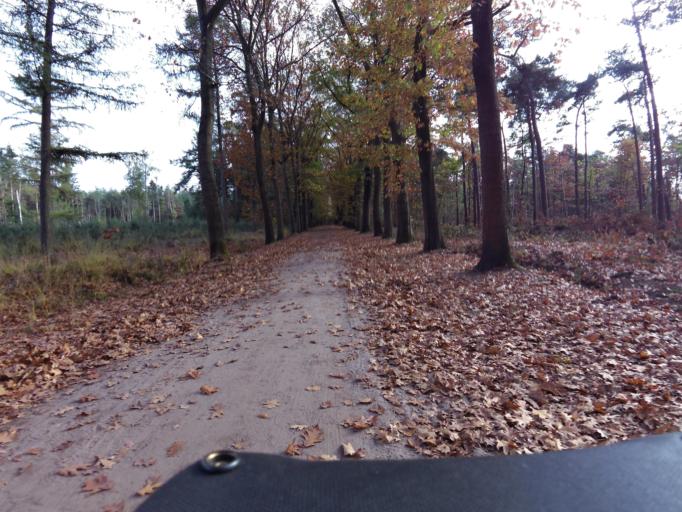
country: NL
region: North Brabant
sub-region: Gemeente Breda
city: Breda
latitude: 51.5402
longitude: 4.7670
